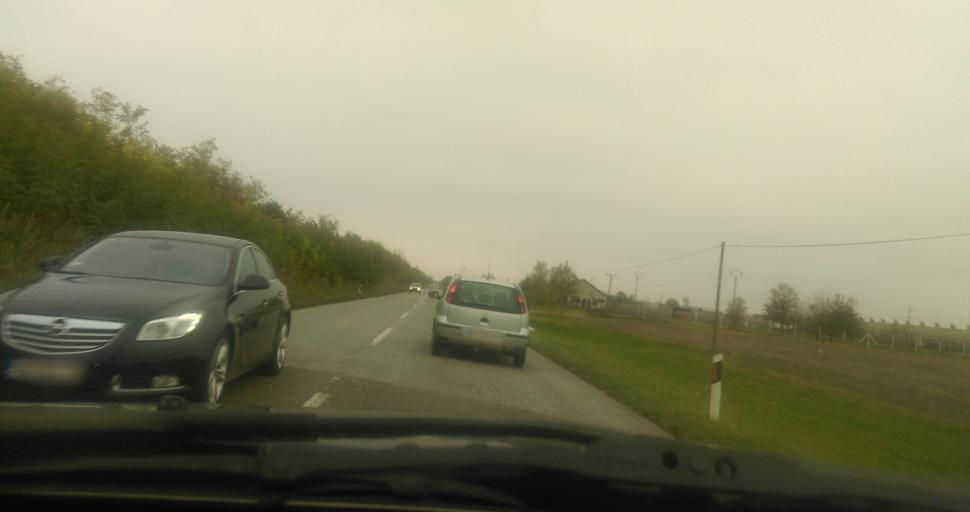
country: RS
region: Autonomna Pokrajina Vojvodina
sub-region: Juznobacki Okrug
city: Becej
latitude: 45.5797
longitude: 20.0270
